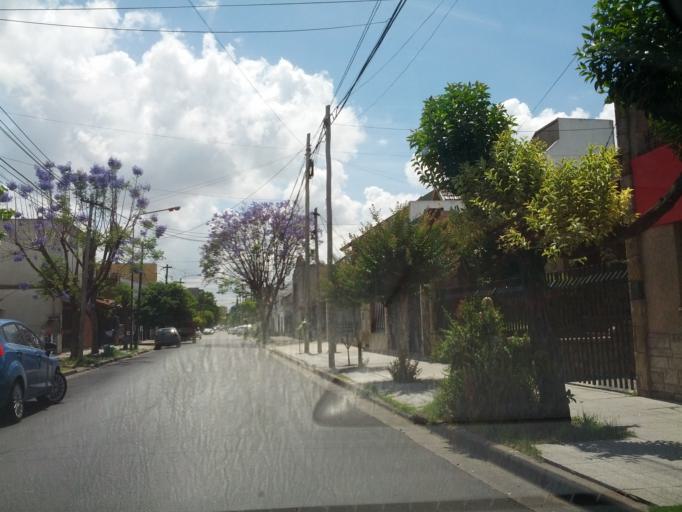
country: AR
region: Buenos Aires
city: San Justo
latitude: -34.6505
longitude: -58.5540
